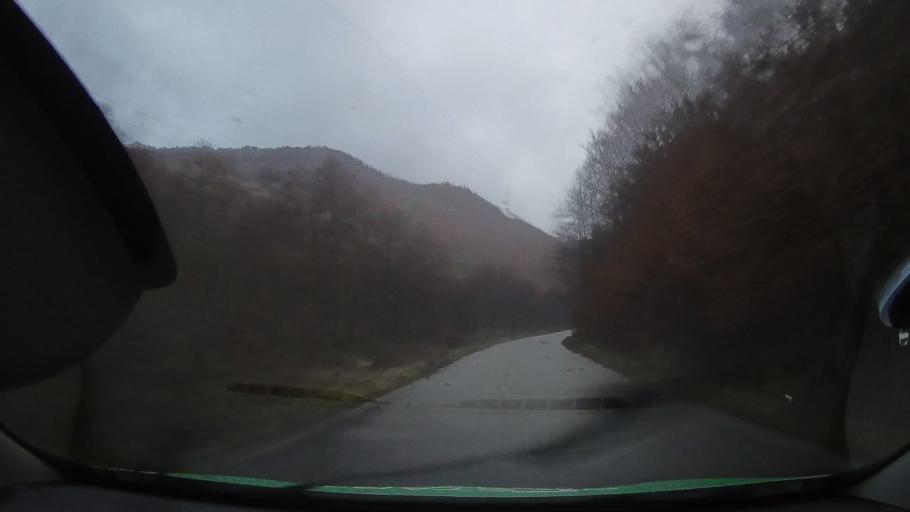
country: RO
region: Hunedoara
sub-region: Comuna Ribita
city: Ribita
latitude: 46.2779
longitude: 22.7405
